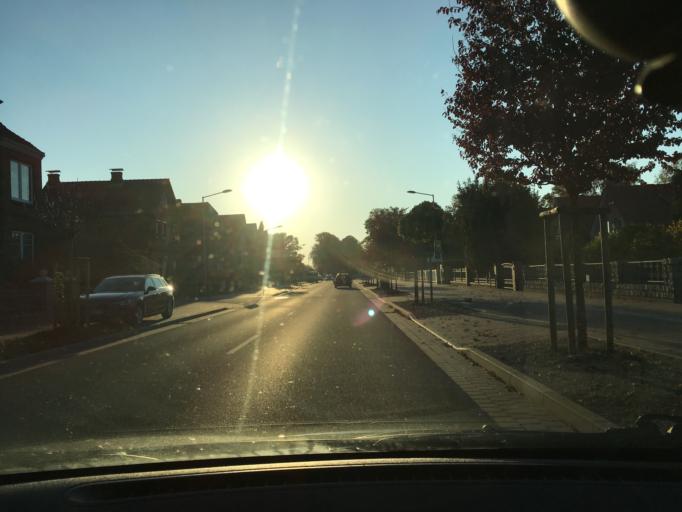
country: DE
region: Mecklenburg-Vorpommern
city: Boizenburg
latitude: 53.3757
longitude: 10.7476
